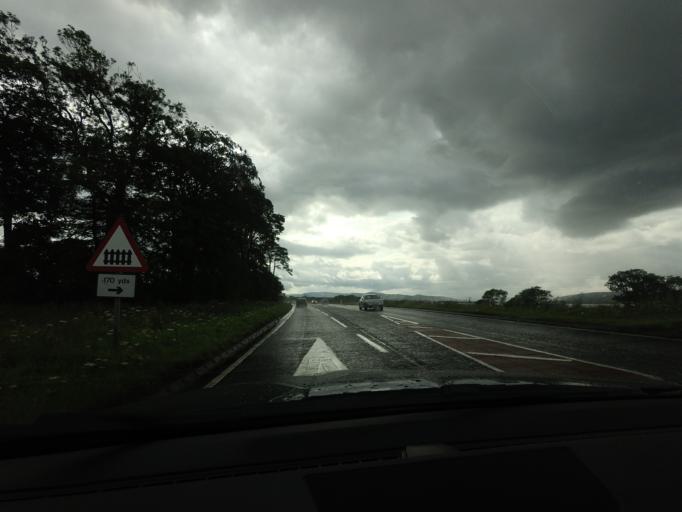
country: GB
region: Scotland
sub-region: Highland
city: Fortrose
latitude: 57.4999
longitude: -4.1443
